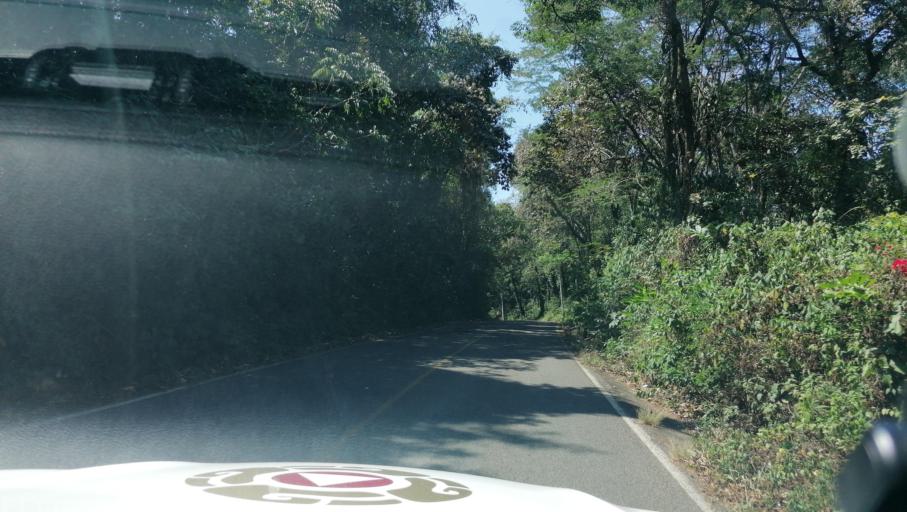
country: MX
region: Chiapas
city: Veinte de Noviembre
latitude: 15.0033
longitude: -92.2301
